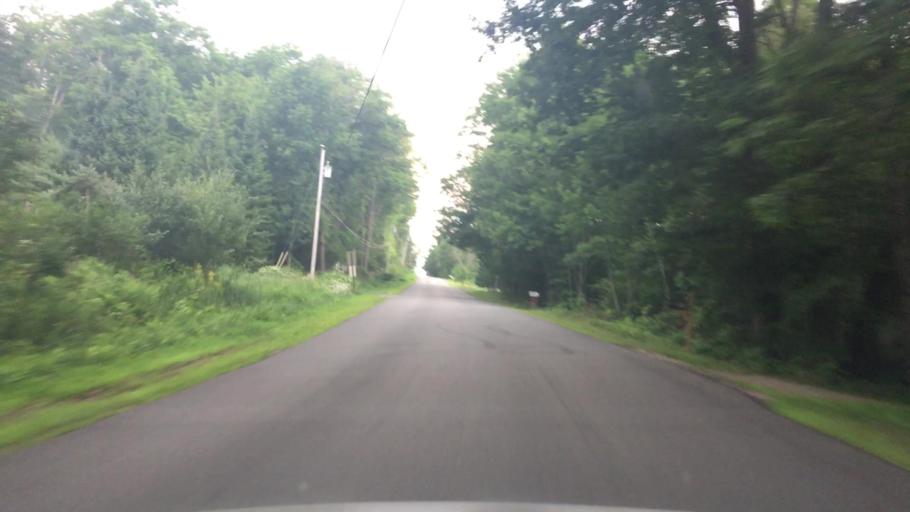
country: US
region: Maine
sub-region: Knox County
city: Washington
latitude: 44.3805
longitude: -69.3516
